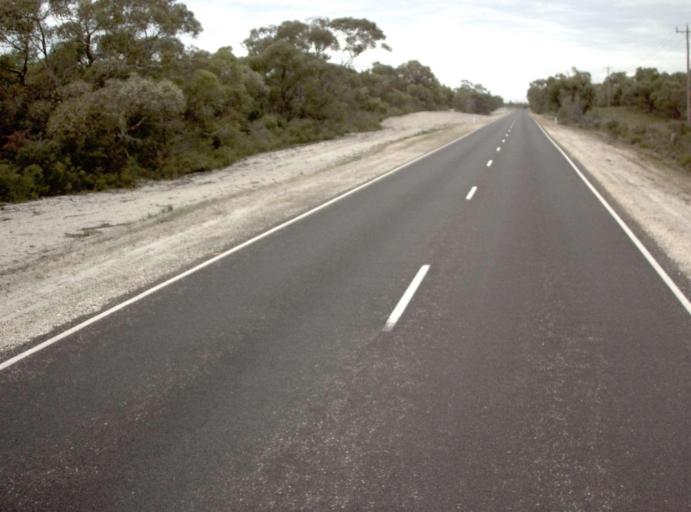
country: AU
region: Victoria
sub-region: Wellington
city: Sale
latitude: -38.1747
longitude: 147.3817
